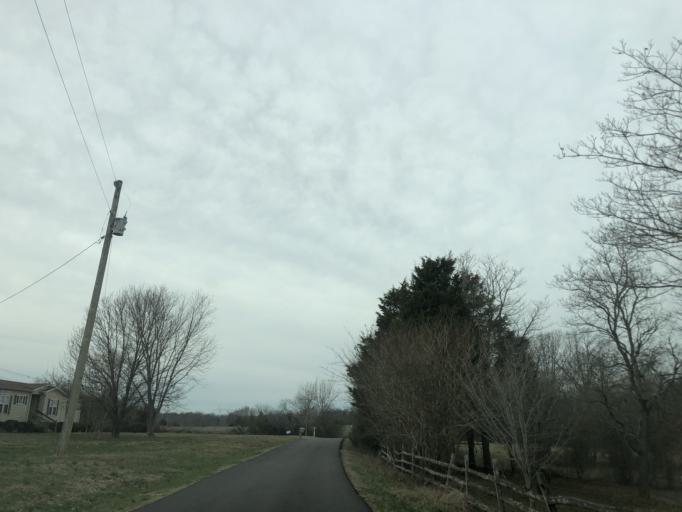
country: US
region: Tennessee
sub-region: Robertson County
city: Greenbrier
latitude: 36.4587
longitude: -86.7851
